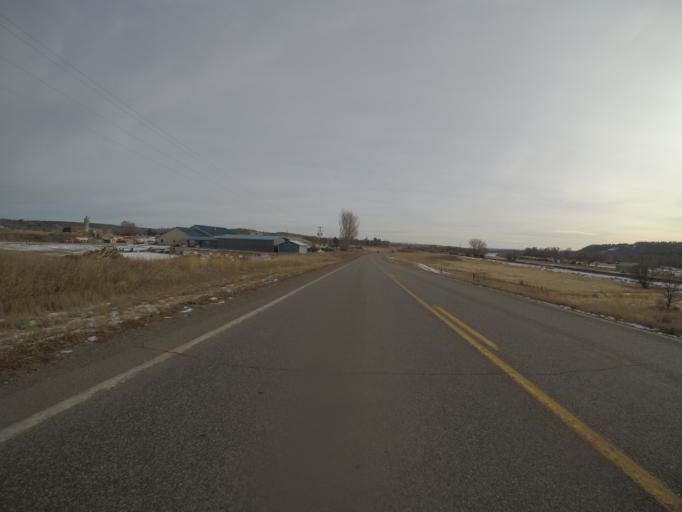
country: US
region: Montana
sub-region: Stillwater County
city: Columbus
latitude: 45.6422
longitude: -109.2828
